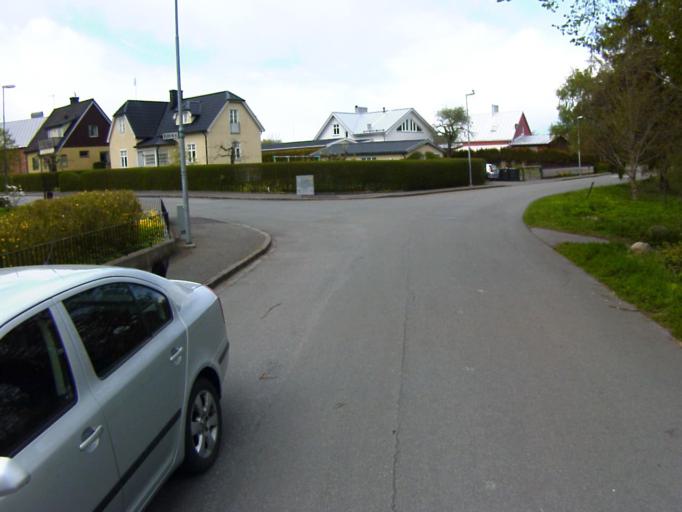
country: SE
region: Skane
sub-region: Kristianstads Kommun
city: Kristianstad
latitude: 56.0368
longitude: 14.1733
